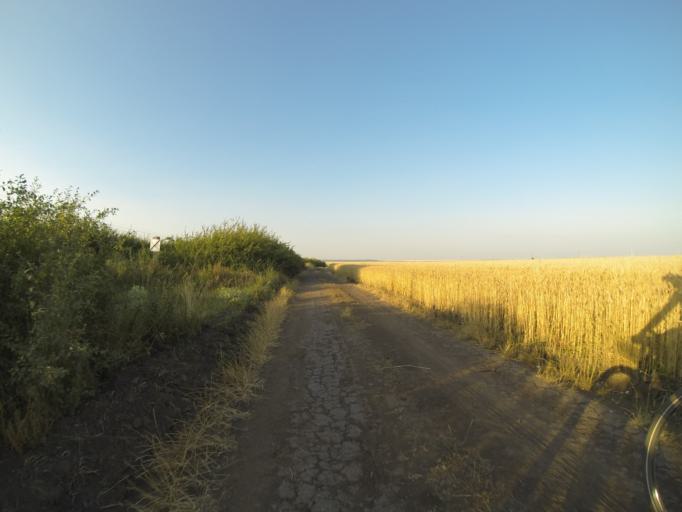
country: RO
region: Dolj
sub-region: Comuna Ceratu
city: Ceratu
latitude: 44.0552
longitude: 23.6774
